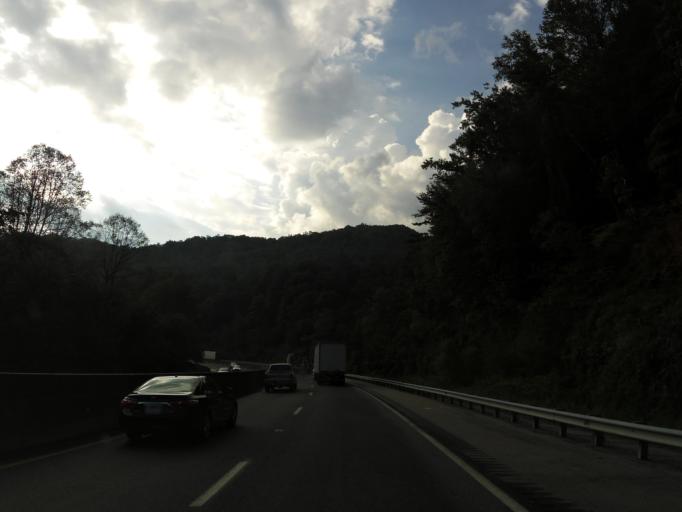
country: US
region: North Carolina
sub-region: Haywood County
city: Cove Creek
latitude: 35.7560
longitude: -83.0345
